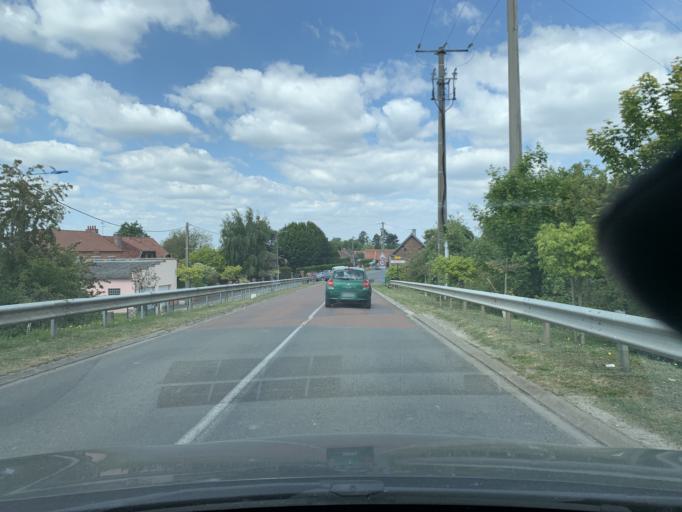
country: FR
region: Nord-Pas-de-Calais
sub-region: Departement du Nord
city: Arleux
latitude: 50.2635
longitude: 3.1022
